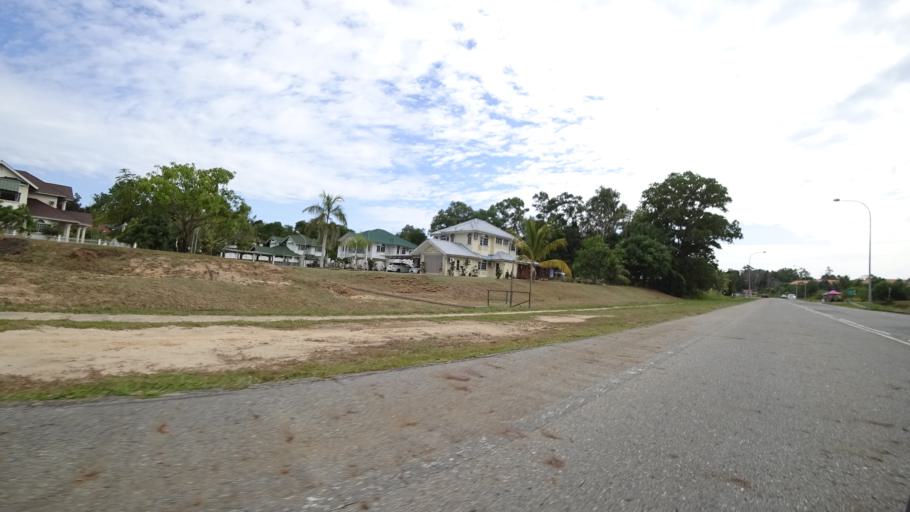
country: BN
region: Brunei and Muara
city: Bandar Seri Begawan
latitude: 4.9636
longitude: 114.9085
